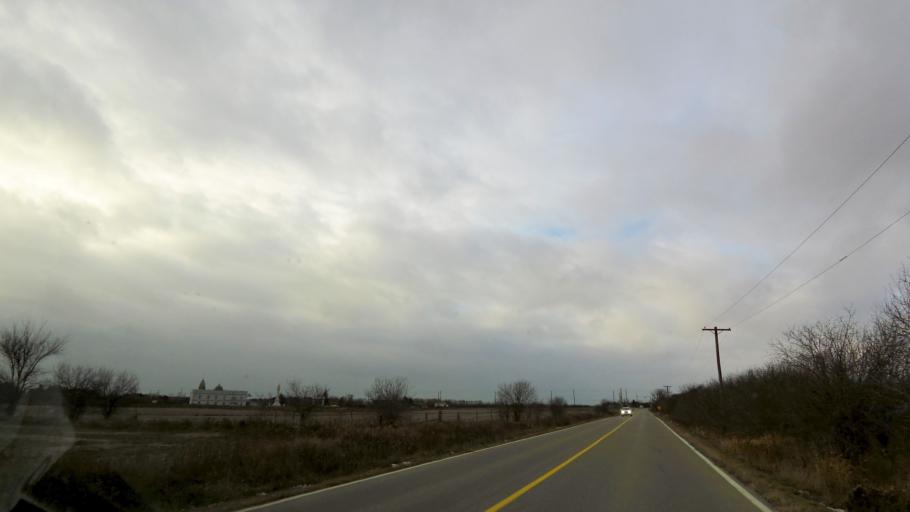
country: CA
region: Ontario
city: Brampton
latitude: 43.8267
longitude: -79.7133
